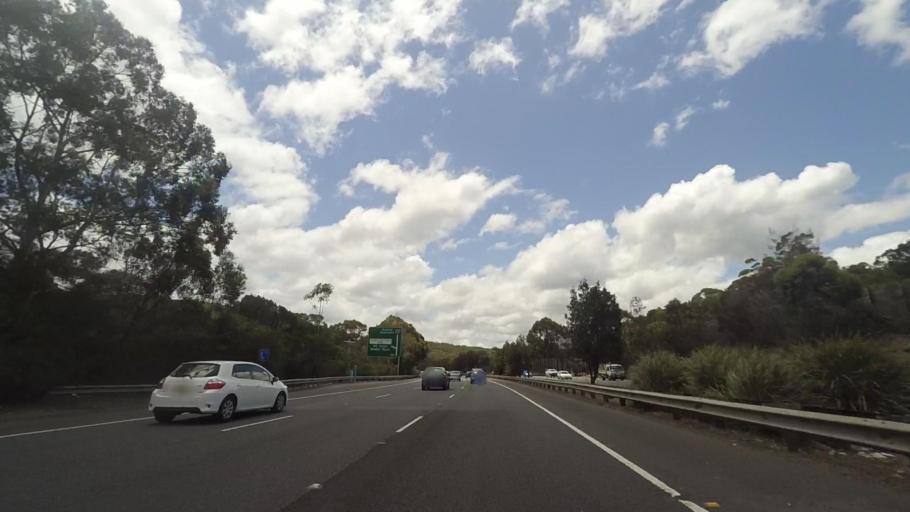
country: AU
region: New South Wales
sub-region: Ku-ring-gai
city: North Wahroonga
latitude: -33.6952
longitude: 151.1209
